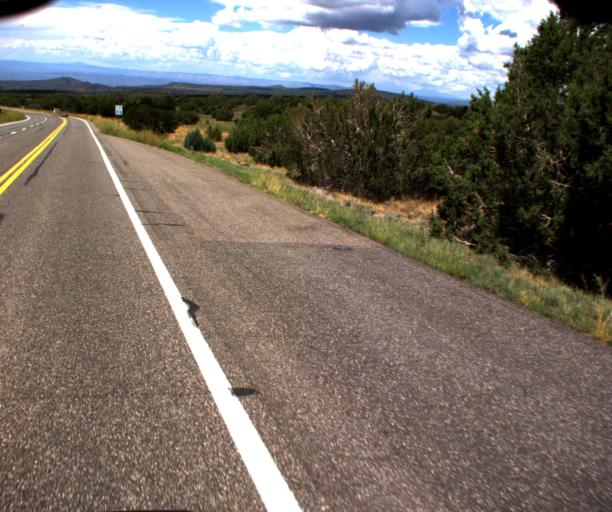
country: US
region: Arizona
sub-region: Gila County
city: Pine
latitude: 34.4908
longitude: -111.6264
